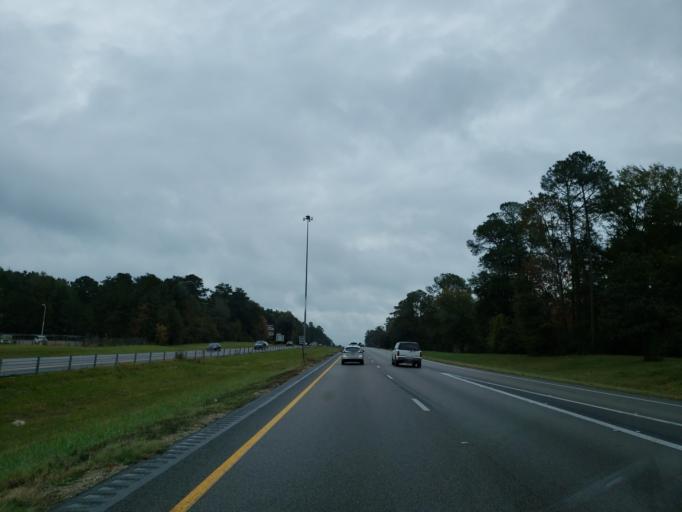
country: US
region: Mississippi
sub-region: Jones County
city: Ellisville
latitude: 31.6152
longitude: -89.2050
